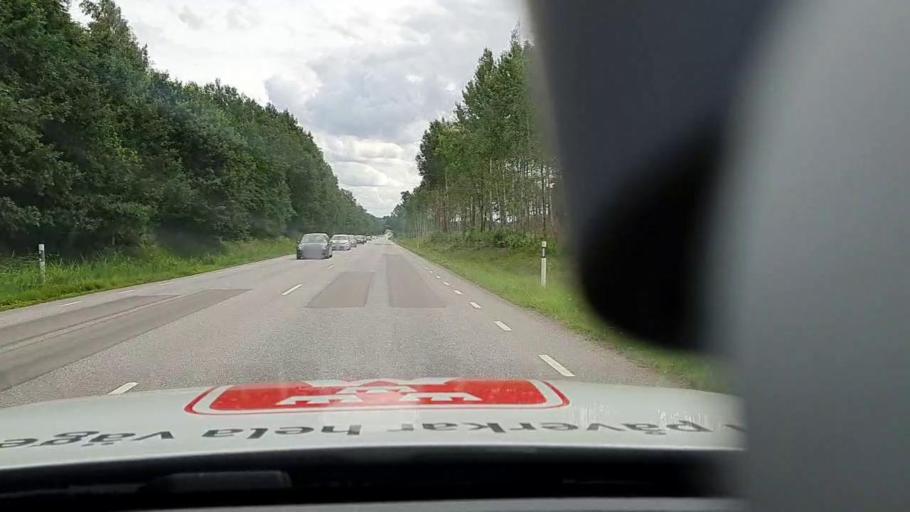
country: SE
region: Vaestra Goetaland
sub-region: Lidkopings Kommun
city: Lidkoping
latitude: 58.5284
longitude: 13.1111
